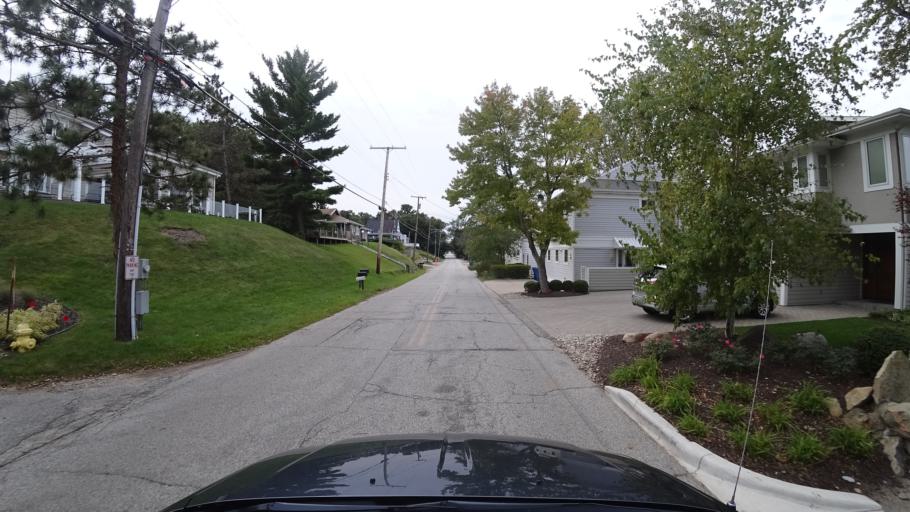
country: US
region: Indiana
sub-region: LaPorte County
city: Long Beach
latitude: 41.7415
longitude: -86.8654
